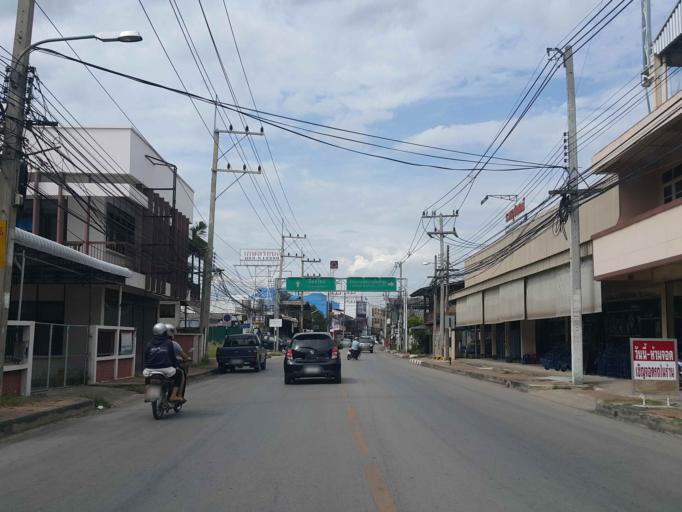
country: TH
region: Lamphun
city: Lamphun
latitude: 18.5861
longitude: 99.0098
